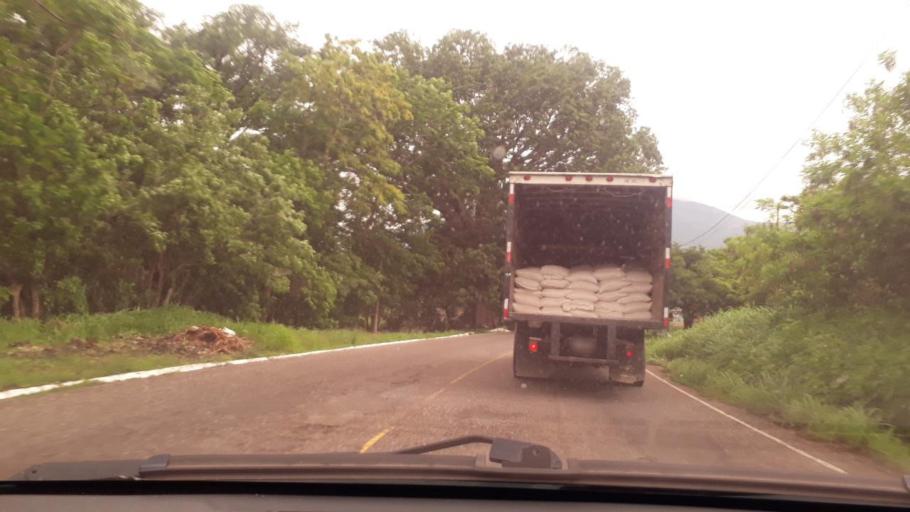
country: GT
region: Jutiapa
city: Santa Catarina Mita
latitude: 14.4684
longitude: -89.7160
